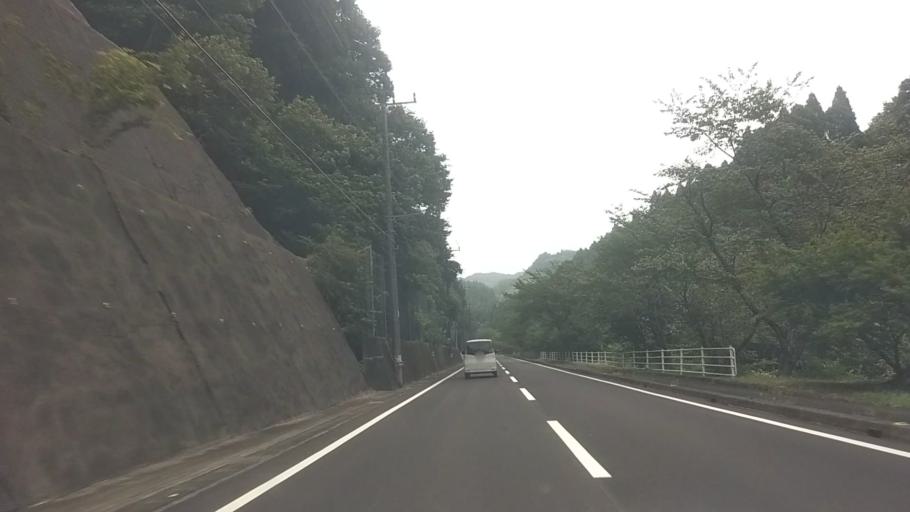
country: JP
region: Chiba
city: Kawaguchi
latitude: 35.2361
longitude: 140.1625
